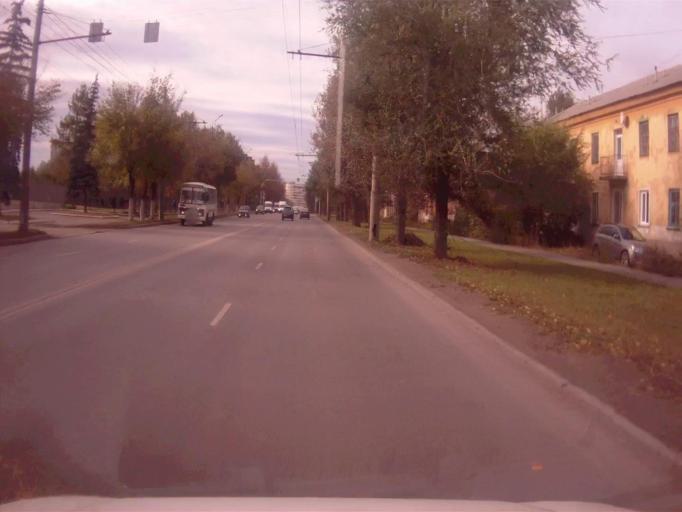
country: RU
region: Chelyabinsk
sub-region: Gorod Chelyabinsk
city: Chelyabinsk
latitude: 55.1147
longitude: 61.4528
